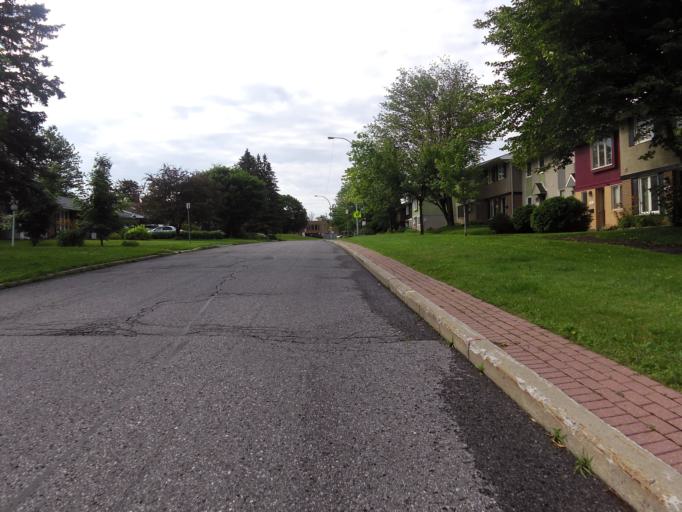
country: CA
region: Ontario
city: Bells Corners
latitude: 45.3352
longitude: -75.7947
